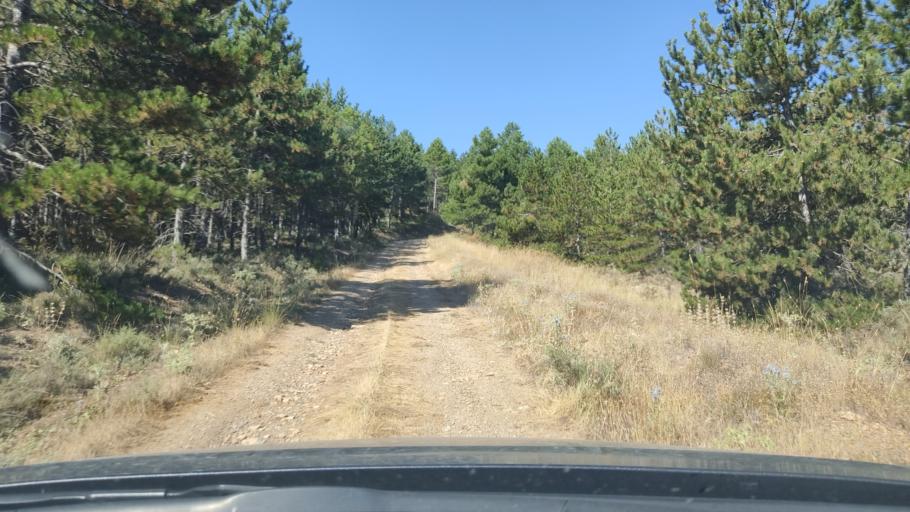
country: ES
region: Aragon
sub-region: Provincia de Teruel
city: Monforte de Moyuela
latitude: 41.0419
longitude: -1.0404
